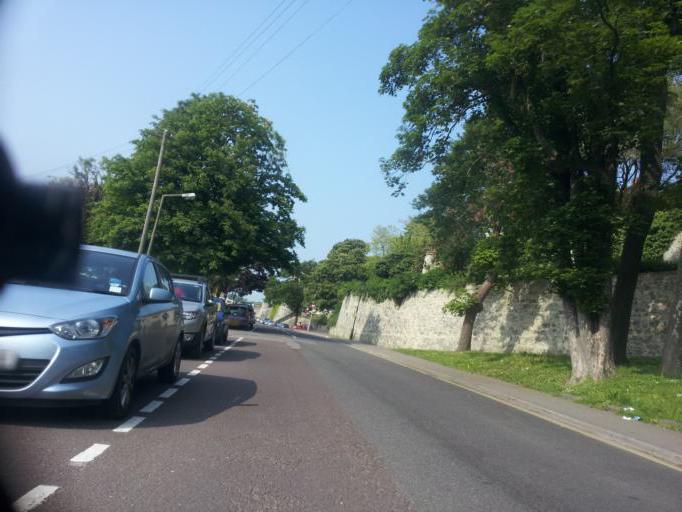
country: GB
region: England
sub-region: Medway
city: Rochester
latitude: 51.3886
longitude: 0.4996
